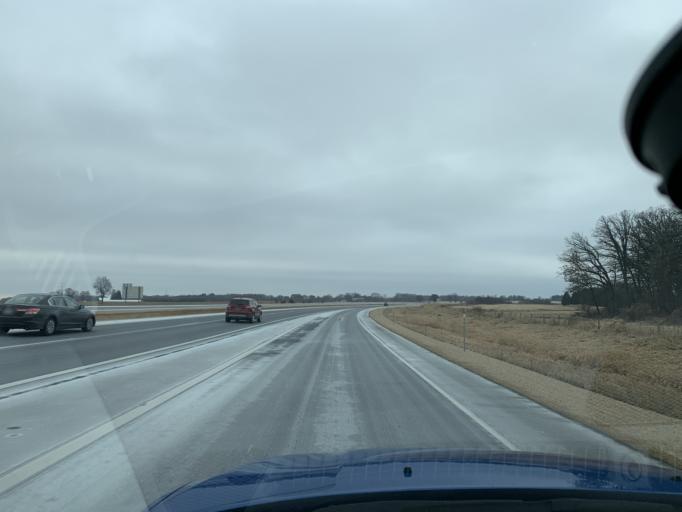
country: US
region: Wisconsin
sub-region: Columbia County
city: Columbus
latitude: 43.3127
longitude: -89.0459
